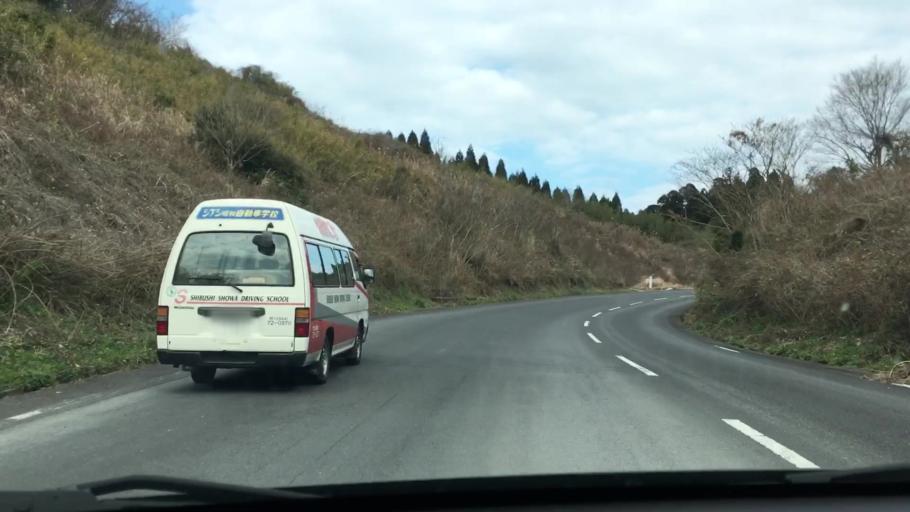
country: JP
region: Miyazaki
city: Kushima
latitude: 31.4955
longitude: 131.2298
